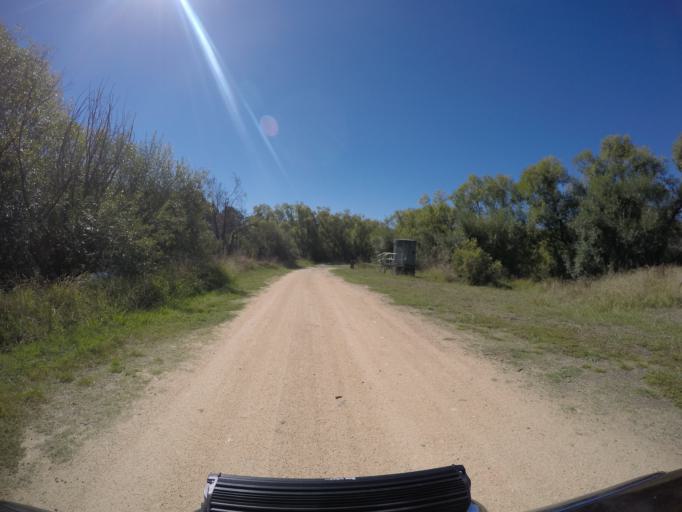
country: AU
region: New South Wales
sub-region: Snowy River
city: Jindabyne
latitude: -36.2173
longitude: 148.1077
